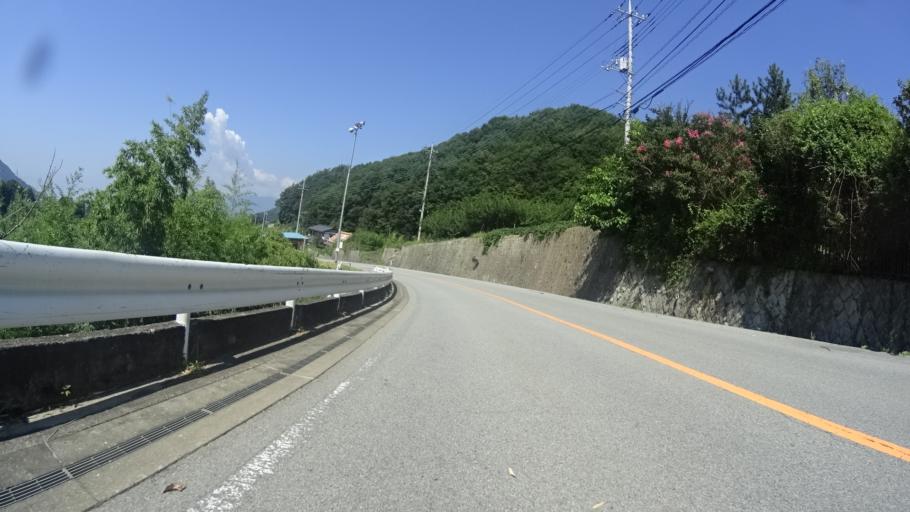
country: JP
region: Yamanashi
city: Enzan
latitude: 35.7335
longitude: 138.7865
